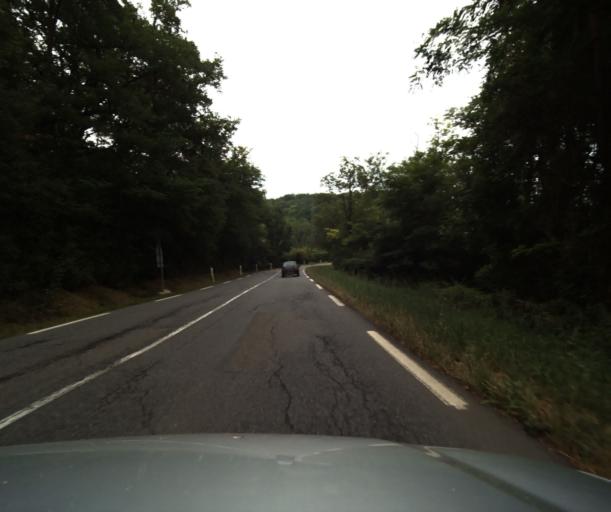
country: FR
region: Midi-Pyrenees
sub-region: Departement du Gers
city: Mielan
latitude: 43.4744
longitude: 0.3331
